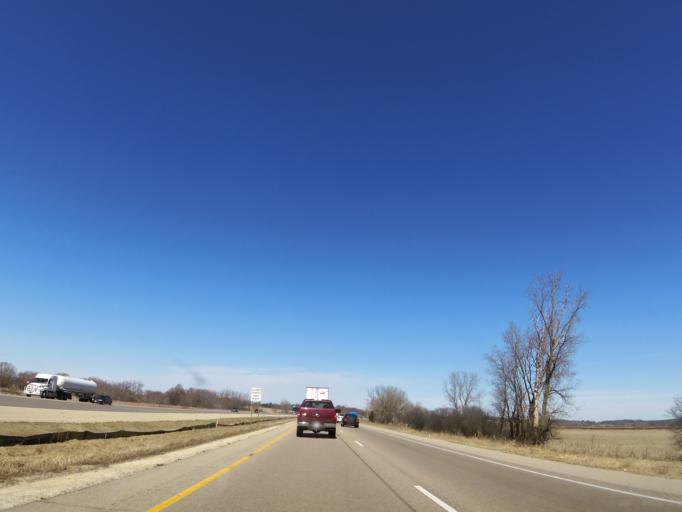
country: US
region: Wisconsin
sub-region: Rock County
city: Edgerton
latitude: 42.9030
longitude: -89.0813
